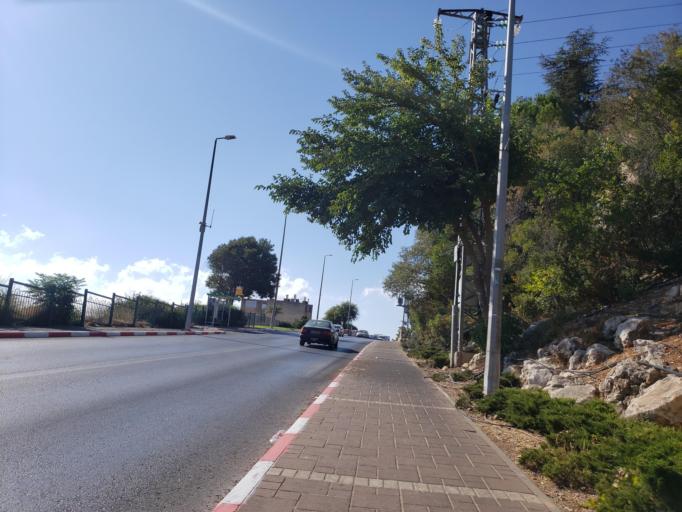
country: IL
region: Northern District
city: Safed
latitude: 32.9654
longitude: 35.4976
